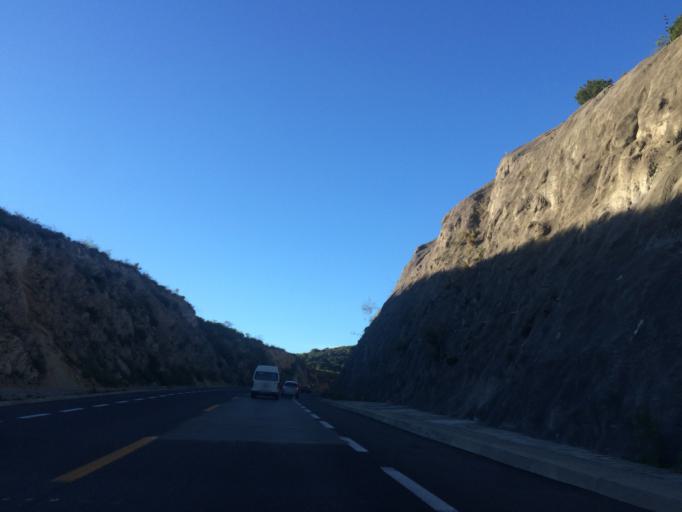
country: MX
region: Puebla
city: Chapuco
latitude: 18.6547
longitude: -97.4538
